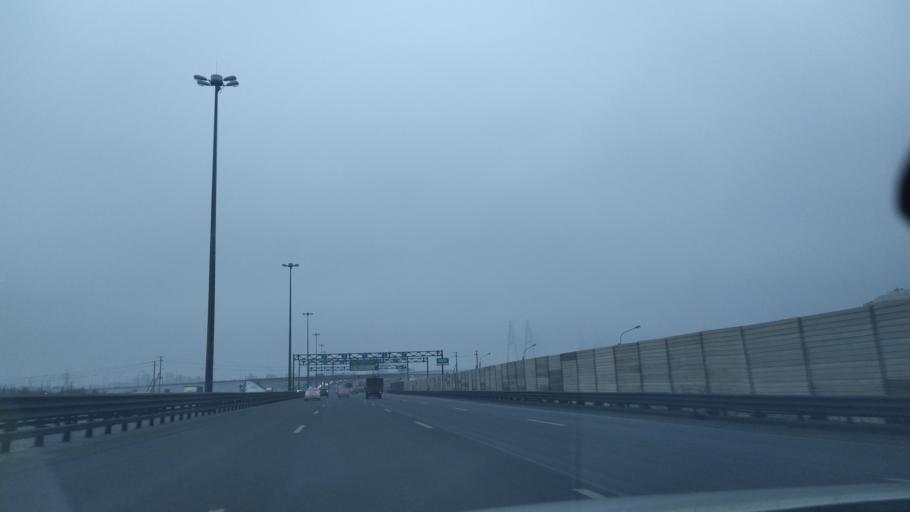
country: RU
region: Leningrad
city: Rybatskoye
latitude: 59.8599
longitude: 30.5166
